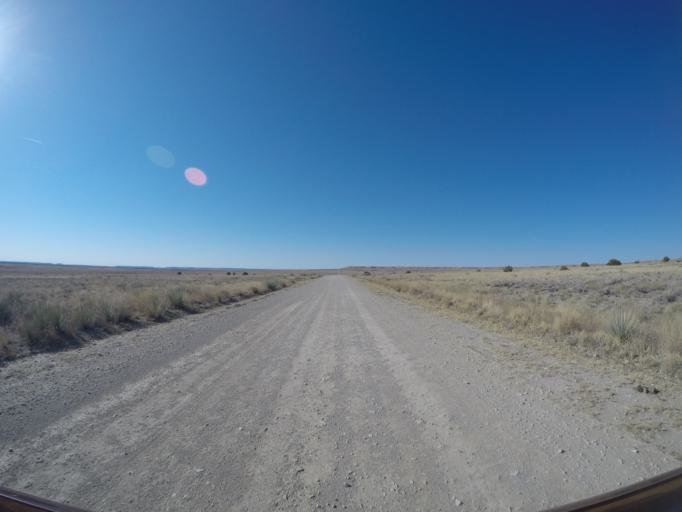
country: US
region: Colorado
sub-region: Otero County
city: La Junta
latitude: 37.7803
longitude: -103.5431
